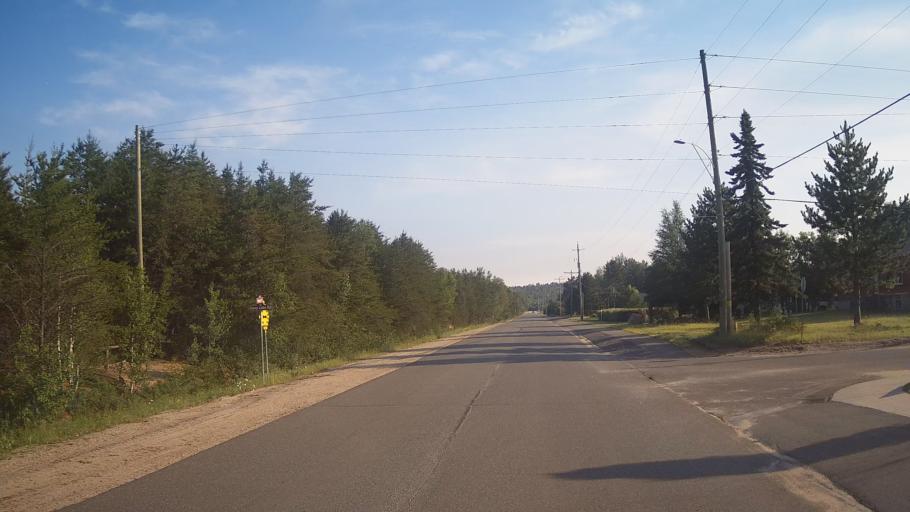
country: CA
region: Ontario
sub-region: Rainy River District
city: Atikokan
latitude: 49.4099
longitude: -91.6661
